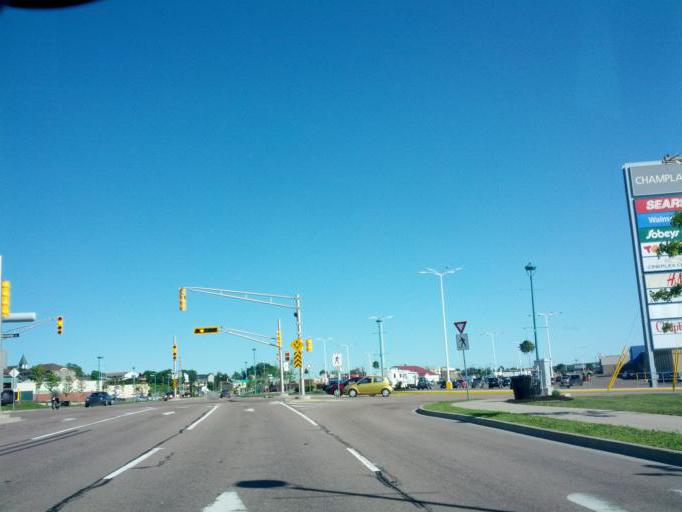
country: CA
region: New Brunswick
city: Moncton
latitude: 46.0990
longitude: -64.7609
